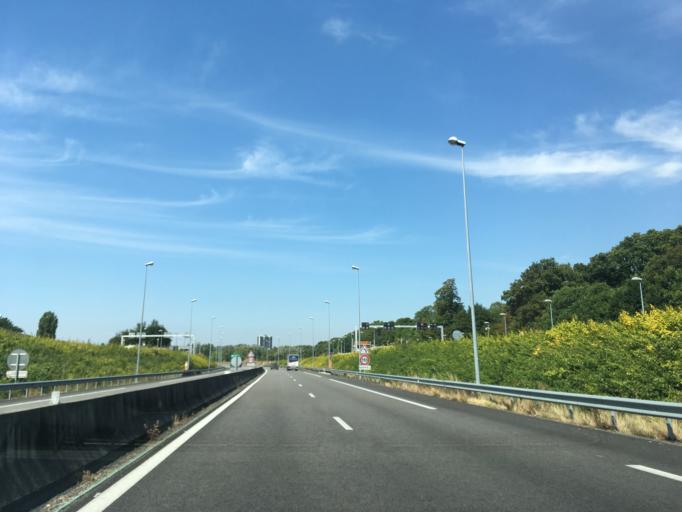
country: FR
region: Ile-de-France
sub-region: Departement des Yvelines
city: Chambourcy
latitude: 48.9112
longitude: 2.0471
